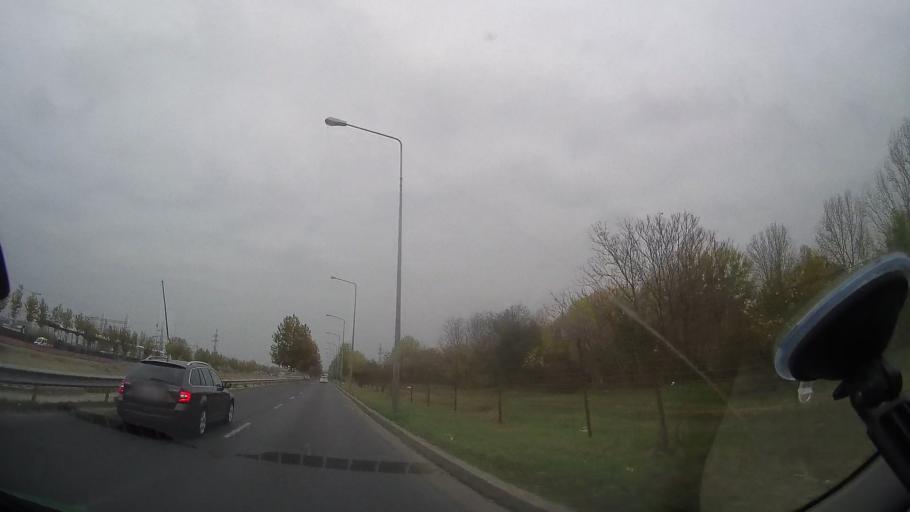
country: RO
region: Ilfov
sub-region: Comuna Popesti-Leordeni
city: Popesti-Leordeni
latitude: 44.4006
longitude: 26.1531
